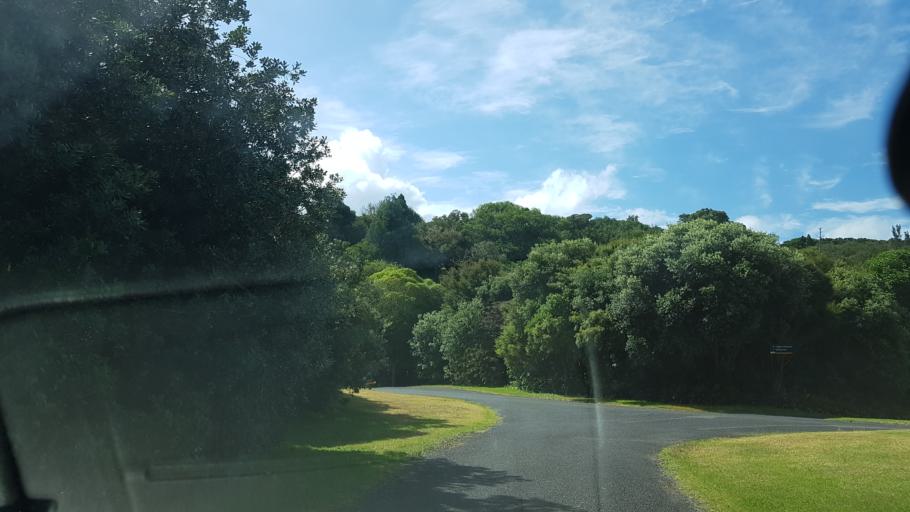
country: NZ
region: Auckland
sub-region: Auckland
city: Rothesay Bay
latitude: -36.6811
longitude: 174.7457
